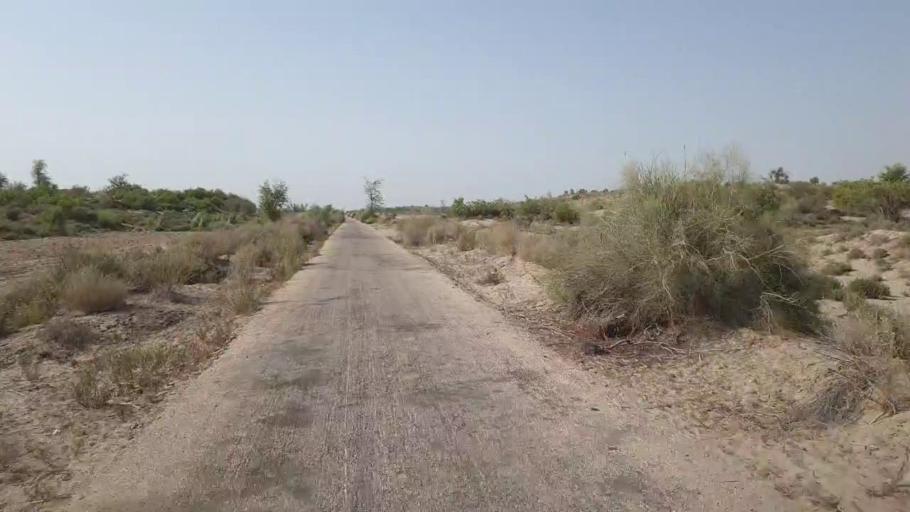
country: PK
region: Sindh
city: Jam Sahib
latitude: 26.5688
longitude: 68.9224
